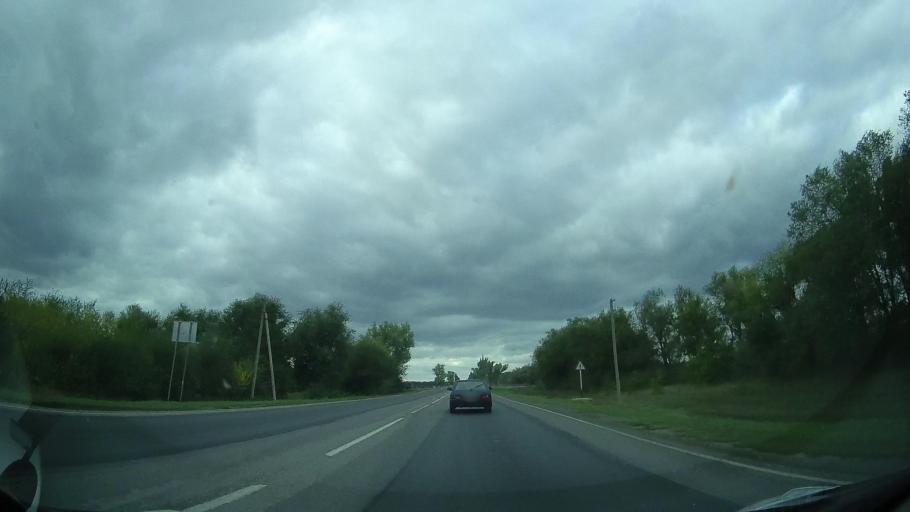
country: RU
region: Rostov
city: Zernograd
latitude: 46.8336
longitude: 40.2345
